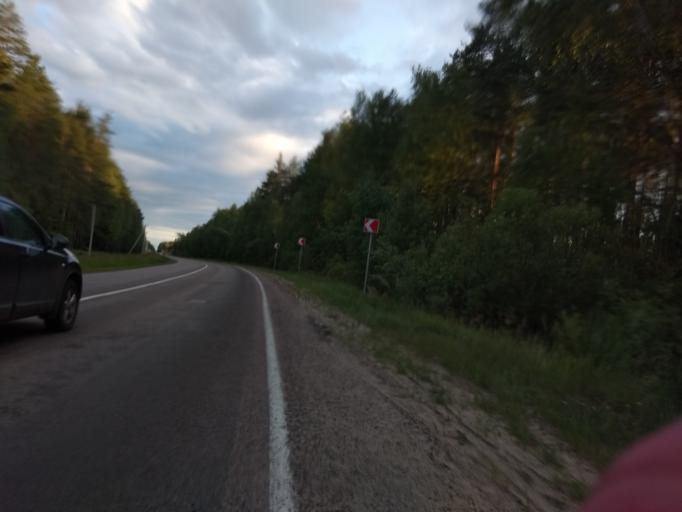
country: RU
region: Moskovskaya
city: Misheronskiy
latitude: 55.6250
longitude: 39.7343
